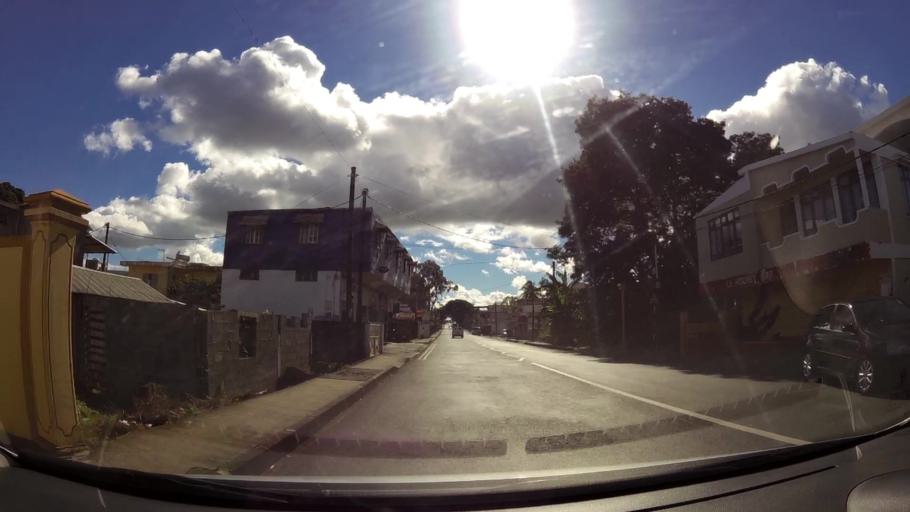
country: MU
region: Pamplemousses
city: Le Hochet
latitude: -20.1380
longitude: 57.5262
